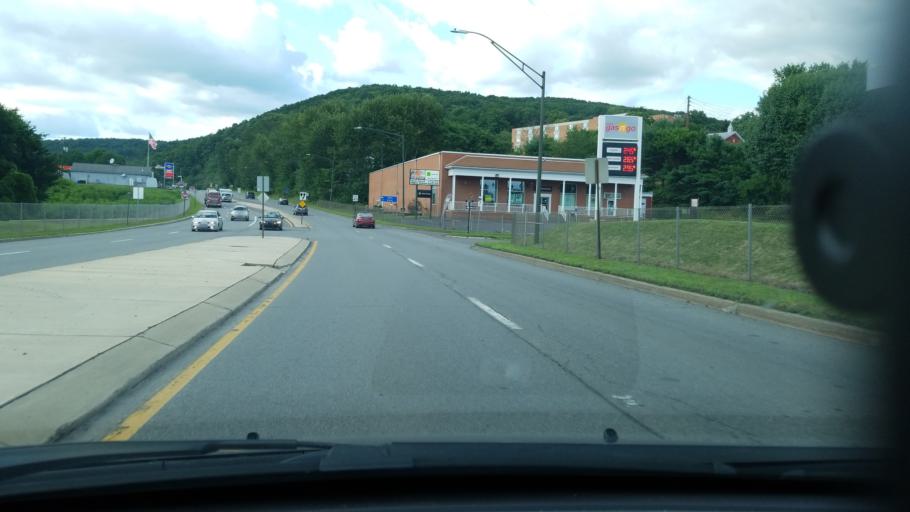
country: US
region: Pennsylvania
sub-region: Montour County
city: Danville
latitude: 40.9673
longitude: -76.6163
